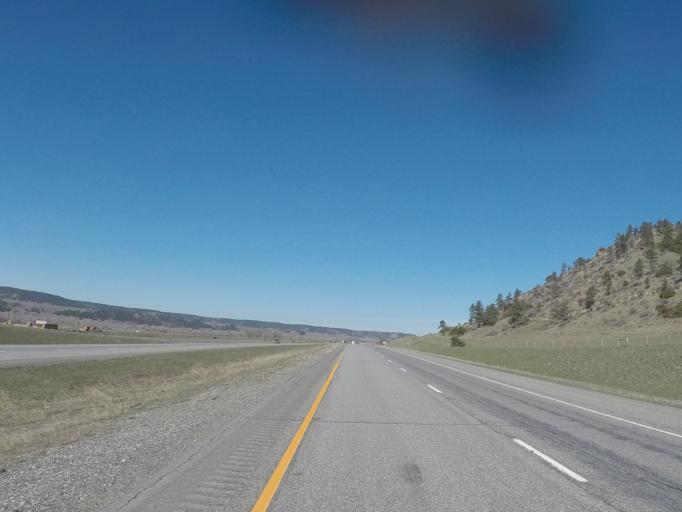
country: US
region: Montana
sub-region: Stillwater County
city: Columbus
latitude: 45.6023
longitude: -109.1337
